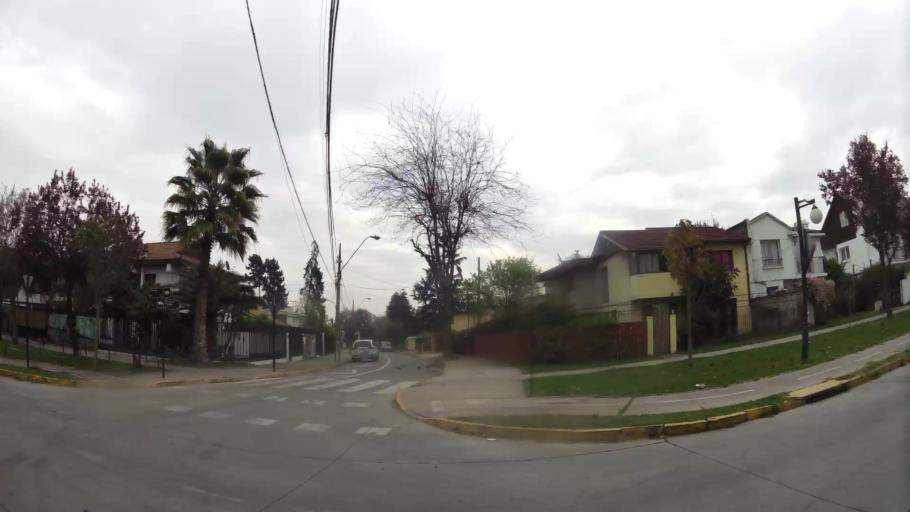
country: CL
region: Santiago Metropolitan
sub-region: Provincia de Santiago
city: Villa Presidente Frei, Nunoa, Santiago, Chile
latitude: -33.4639
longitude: -70.5880
